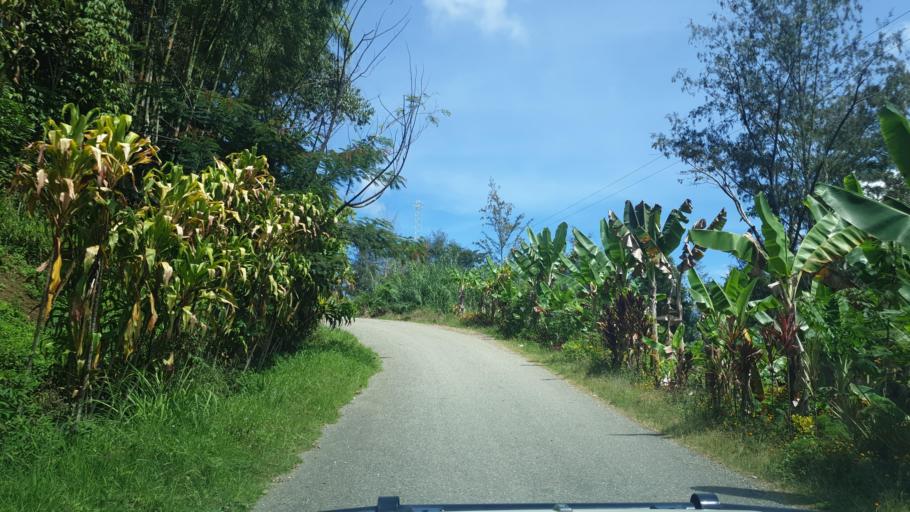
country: PG
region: Chimbu
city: Kundiawa
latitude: -6.1380
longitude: 145.1281
